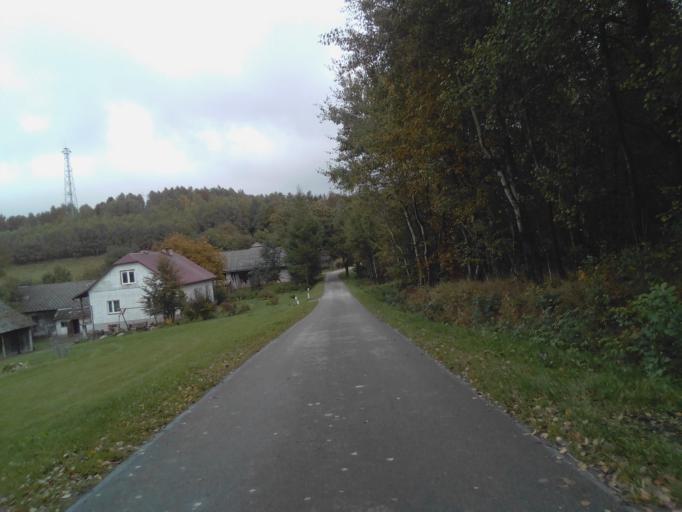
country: PL
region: Subcarpathian Voivodeship
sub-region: Powiat strzyzowski
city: Gwoznica Gorna
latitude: 49.8361
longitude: 22.0192
